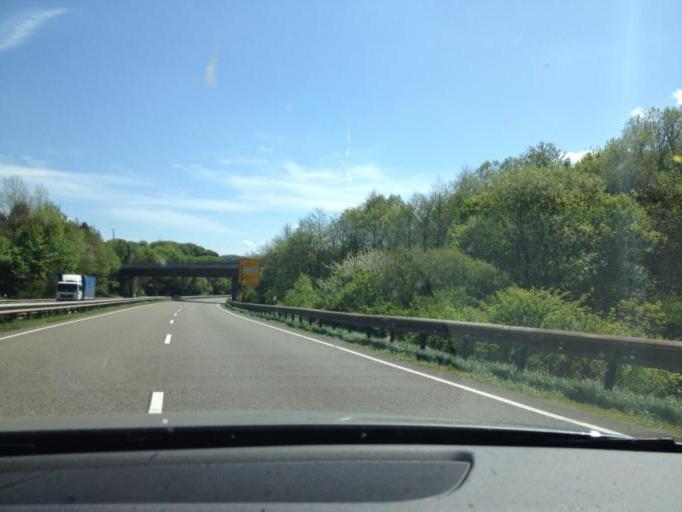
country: DE
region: Rheinland-Pfalz
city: Kerschenbach
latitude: 50.3699
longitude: 6.5099
